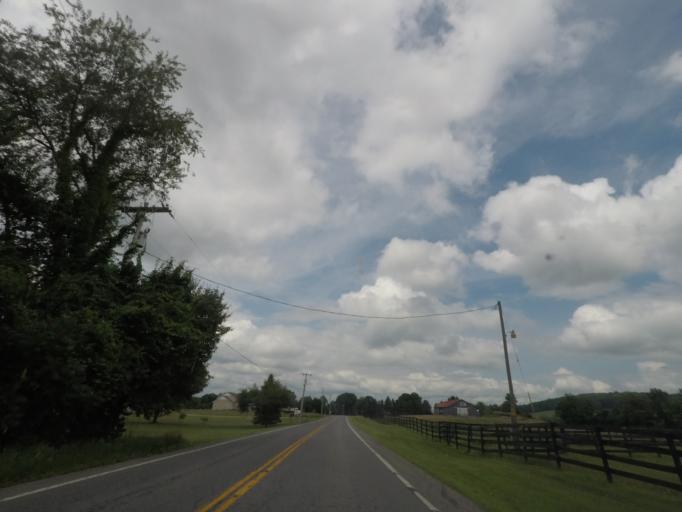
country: US
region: New York
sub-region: Saratoga County
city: Stillwater
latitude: 43.0323
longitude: -73.6856
